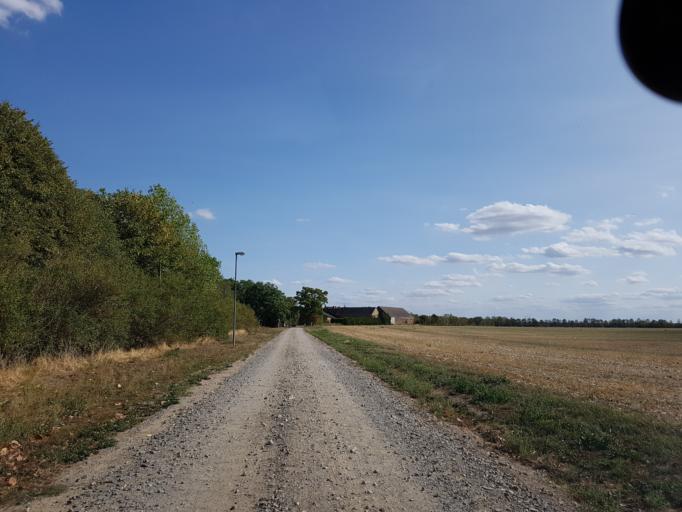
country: DE
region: Brandenburg
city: Treuenbrietzen
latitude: 51.9931
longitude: 12.8578
